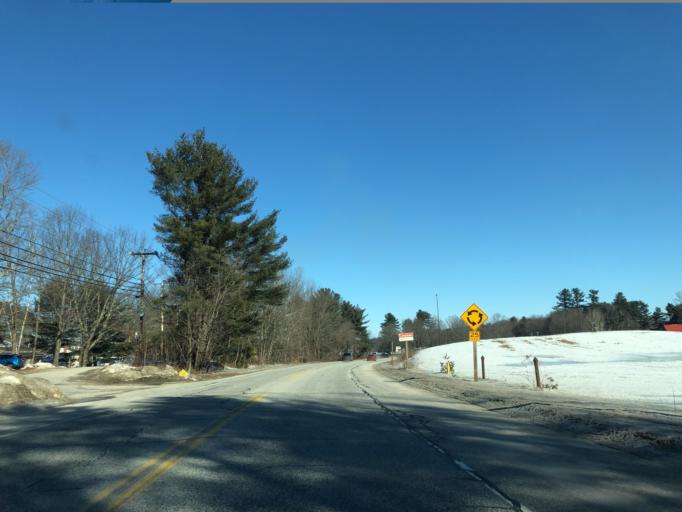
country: US
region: Maine
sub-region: Cumberland County
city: North Windham
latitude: 43.8003
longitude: -70.4074
